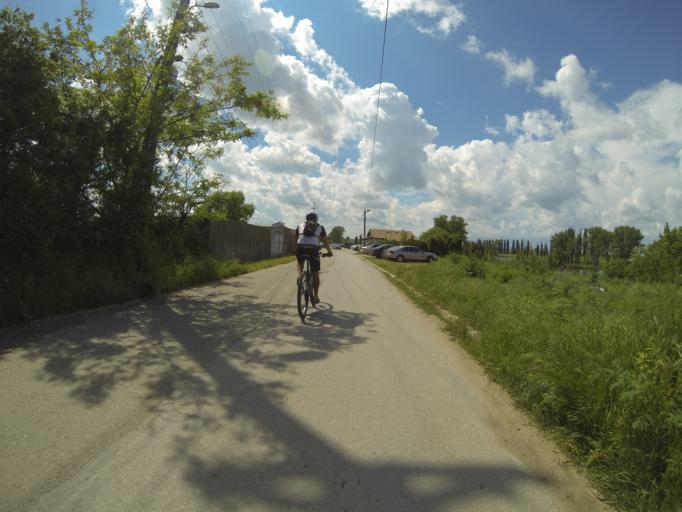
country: RO
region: Dolj
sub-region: Municipiul Craiova
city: Facai
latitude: 44.2682
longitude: 23.8328
